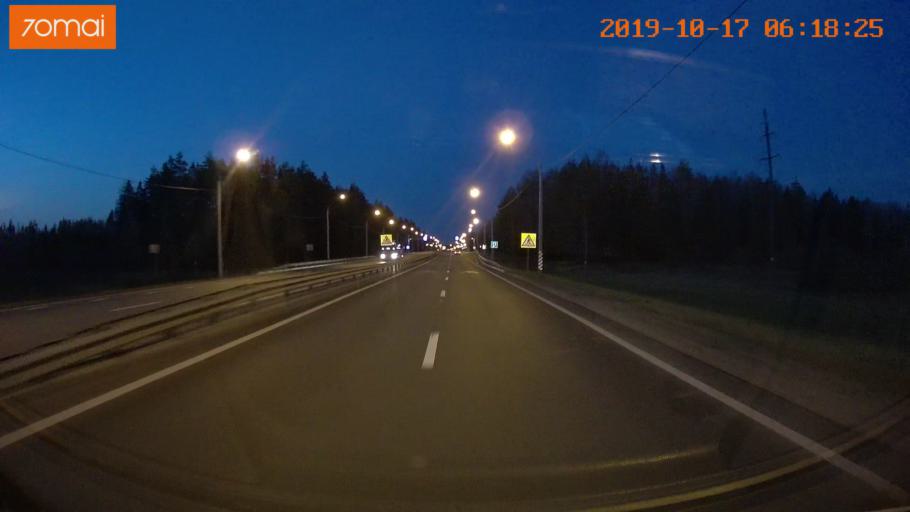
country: RU
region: Ivanovo
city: Lezhnevo
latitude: 56.8417
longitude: 40.9118
